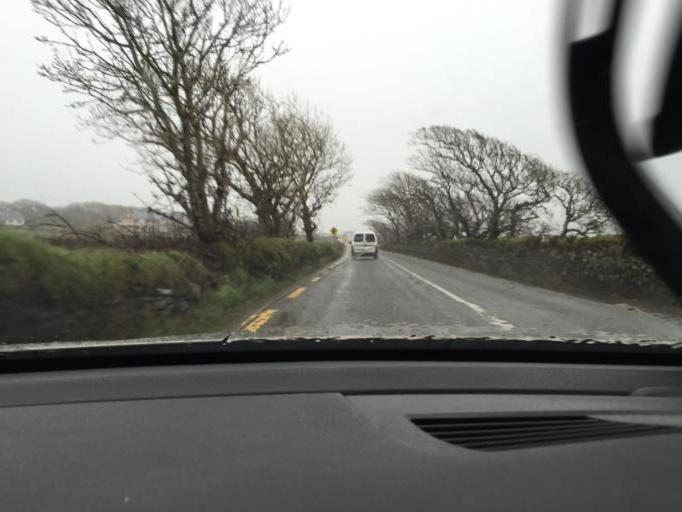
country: IE
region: Munster
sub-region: Ciarrai
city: Dingle
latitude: 52.1312
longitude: -10.2544
